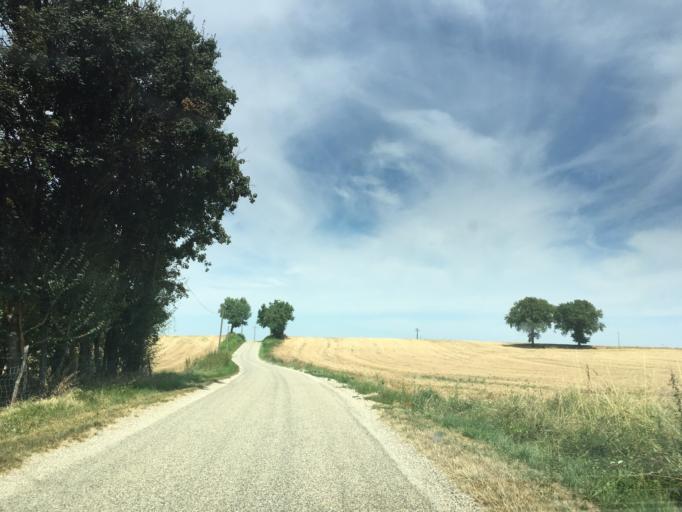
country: FR
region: Midi-Pyrenees
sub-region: Departement du Gers
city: Jegun
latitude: 43.8009
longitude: 0.4980
